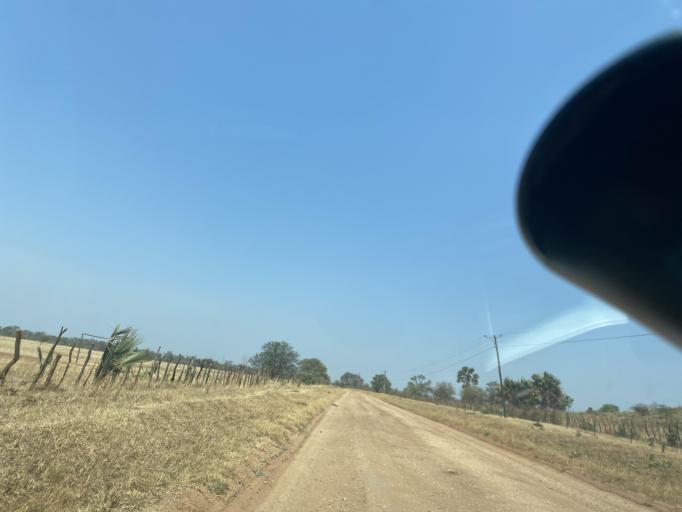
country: ZM
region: Lusaka
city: Lusaka
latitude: -15.5368
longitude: 28.0853
